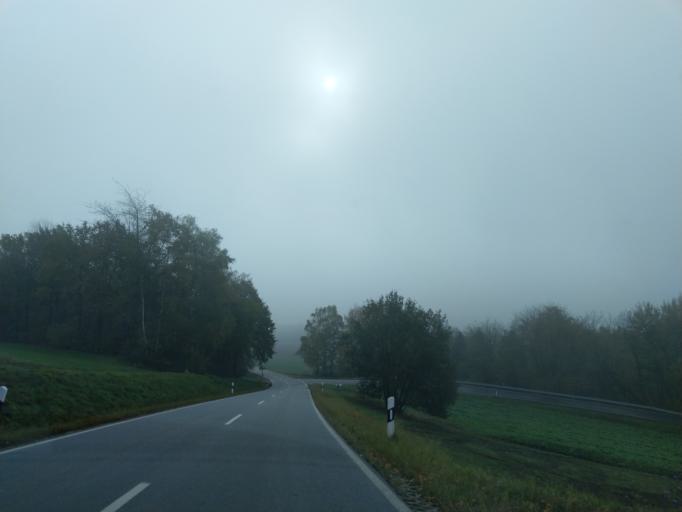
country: DE
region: Bavaria
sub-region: Lower Bavaria
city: Grattersdorf
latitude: 48.7911
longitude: 13.1579
